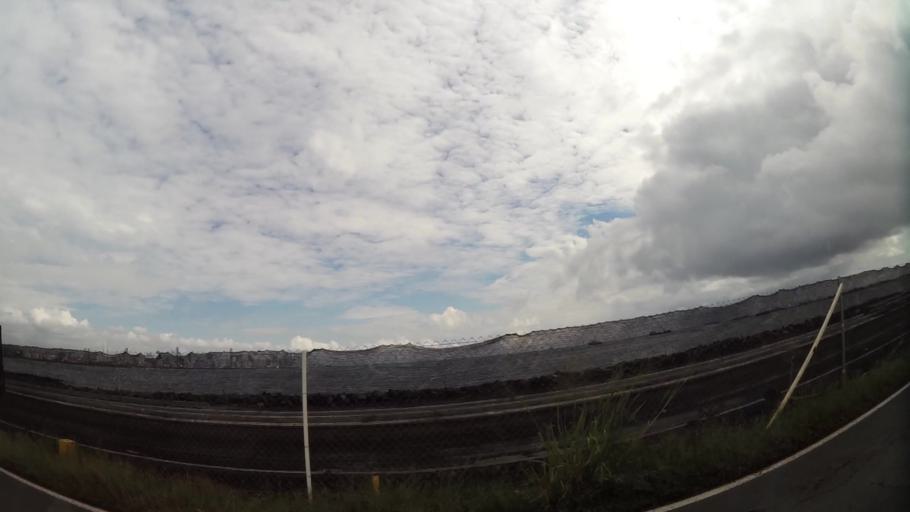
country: PA
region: Panama
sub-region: Distrito de Panama
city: Ancon
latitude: 8.9254
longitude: -79.5403
